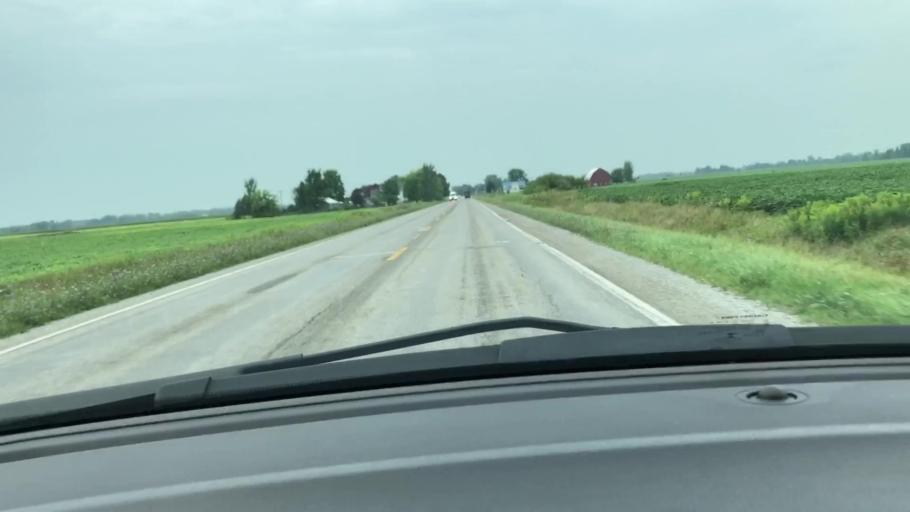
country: US
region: Michigan
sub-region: Bay County
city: Auburn
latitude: 43.5627
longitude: -84.0898
